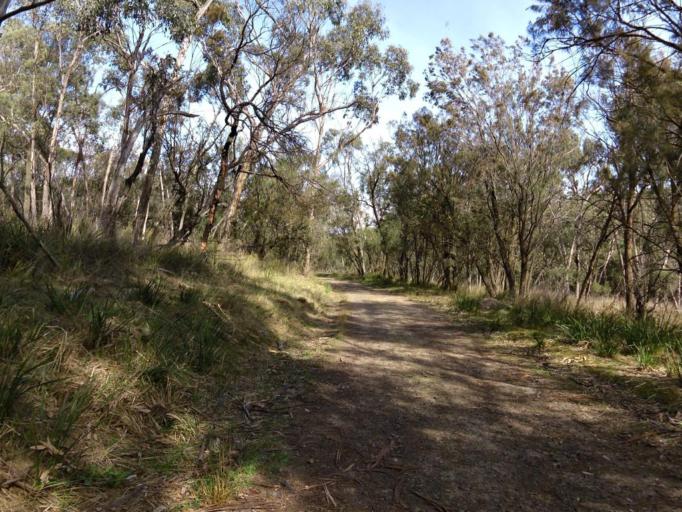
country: AU
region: Victoria
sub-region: Casey
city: Endeavour Hills
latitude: -37.9474
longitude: 145.2625
